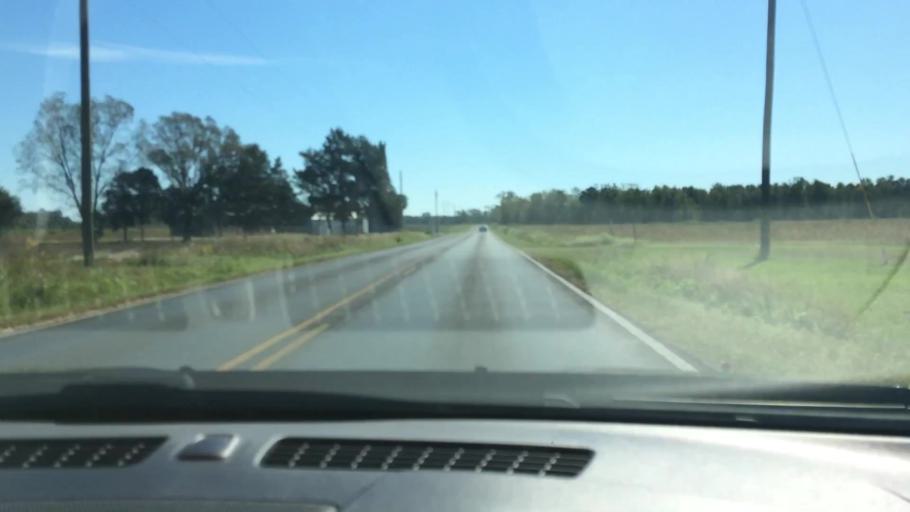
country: US
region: North Carolina
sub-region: Pitt County
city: Grifton
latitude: 35.3740
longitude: -77.3589
